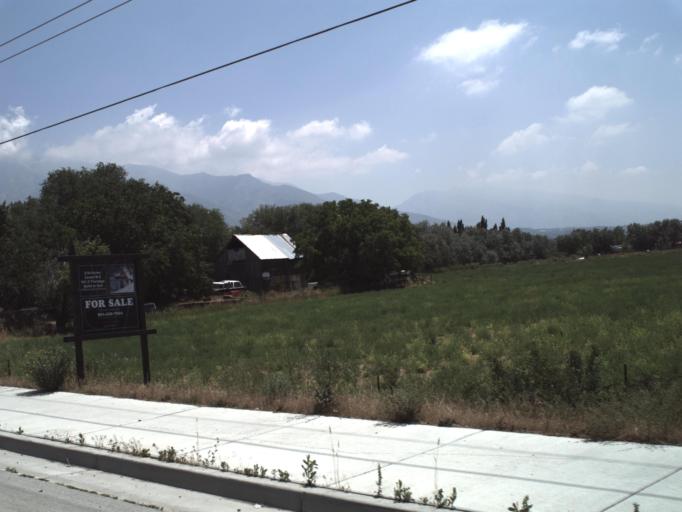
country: US
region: Utah
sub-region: Weber County
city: Marriott-Slaterville
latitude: 41.2444
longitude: -111.9983
